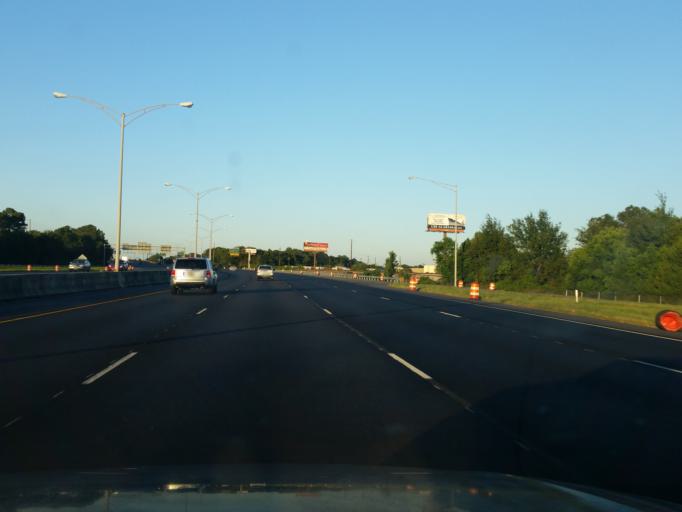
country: US
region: Alabama
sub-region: Mobile County
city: Mobile
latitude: 30.6504
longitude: -88.0736
